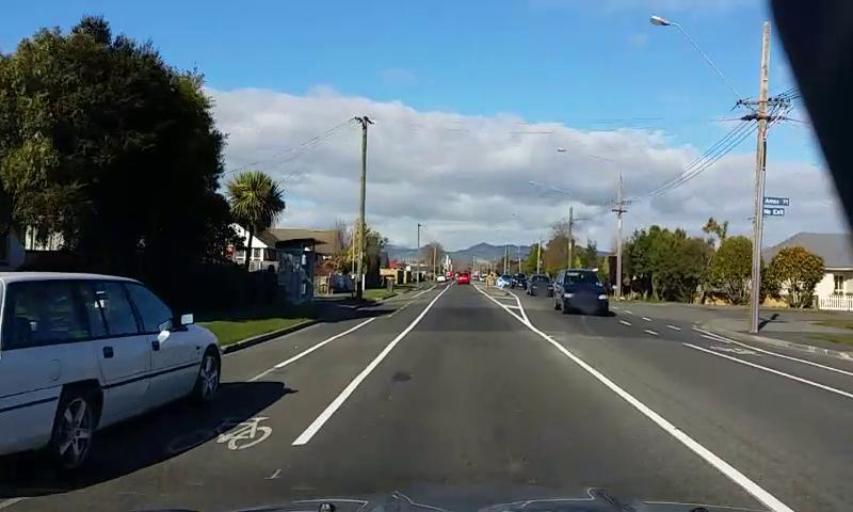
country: NZ
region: Canterbury
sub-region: Christchurch City
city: Christchurch
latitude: -43.5009
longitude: 172.6622
